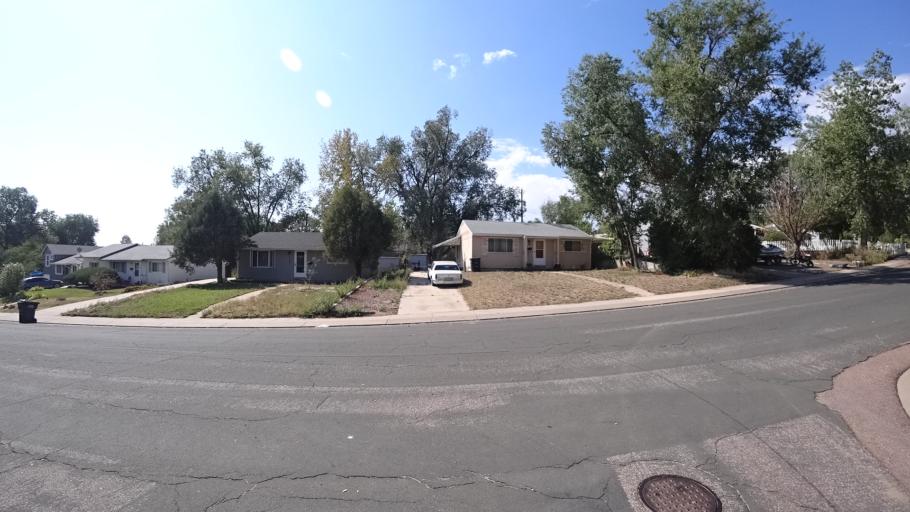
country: US
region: Colorado
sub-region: El Paso County
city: Colorado Springs
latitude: 38.8236
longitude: -104.7890
